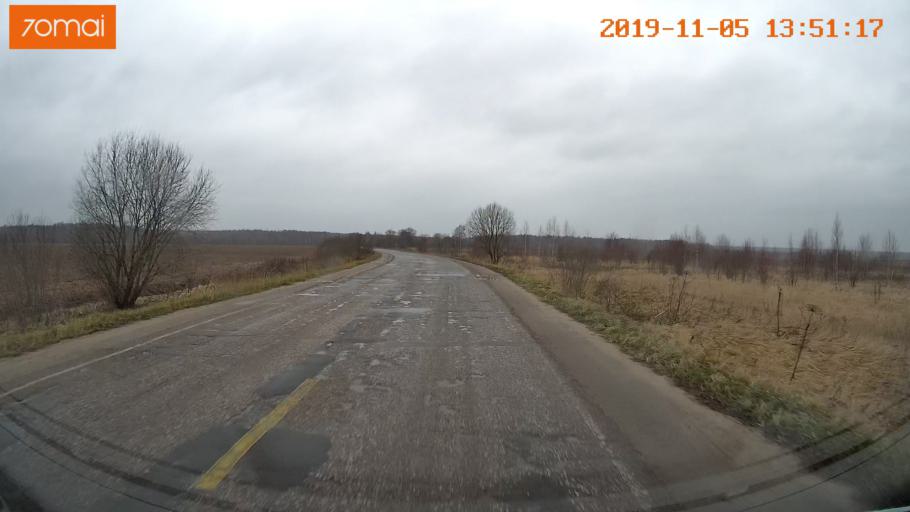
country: RU
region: Ivanovo
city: Kaminskiy
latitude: 57.0244
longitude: 41.4023
